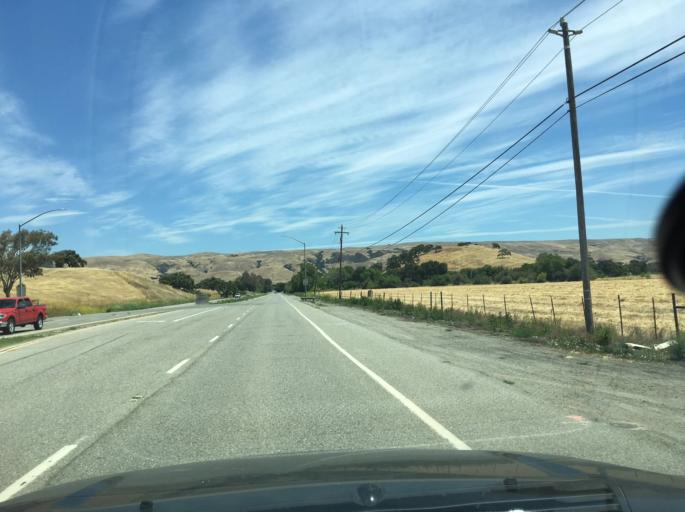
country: US
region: California
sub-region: Santa Clara County
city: Morgan Hill
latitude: 37.1953
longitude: -121.7447
